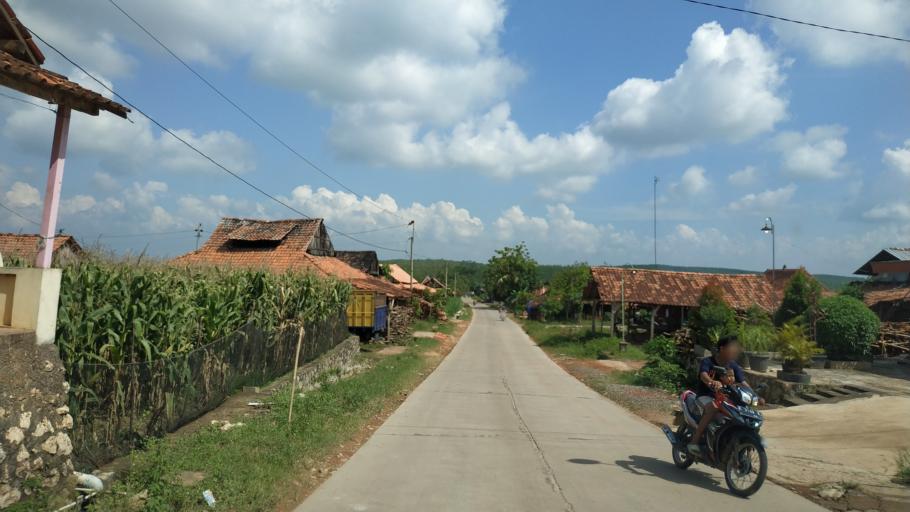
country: ID
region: Central Java
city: Jepang
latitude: -7.0127
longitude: 111.1172
